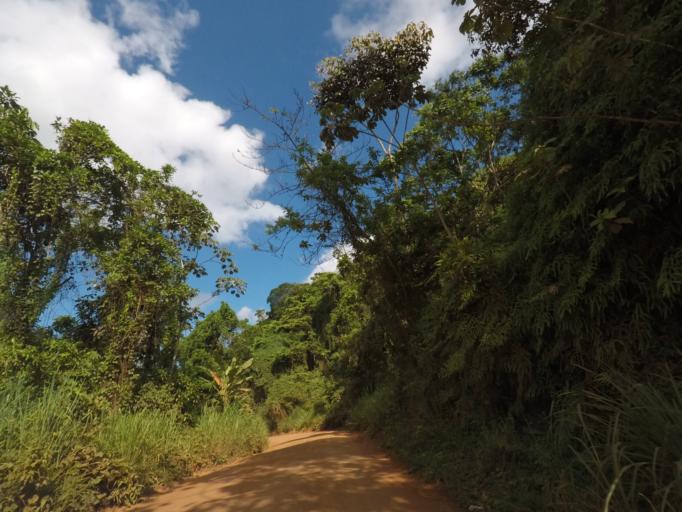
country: BR
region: Bahia
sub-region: Itacare
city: Itacare
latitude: -14.2183
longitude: -39.0701
